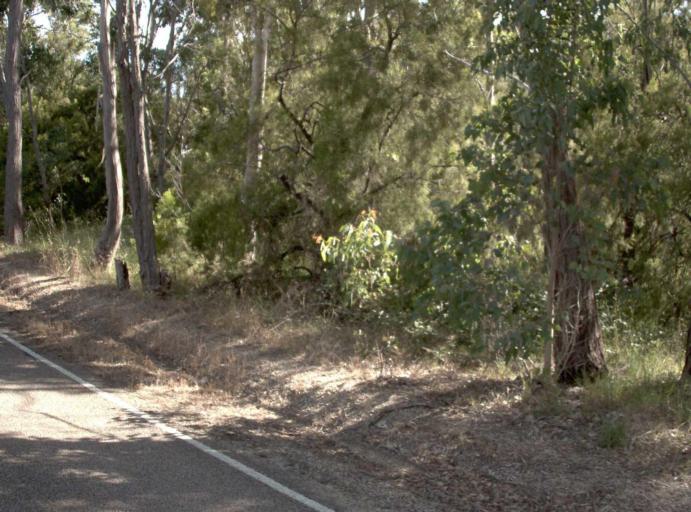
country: AU
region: Victoria
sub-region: East Gippsland
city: Lakes Entrance
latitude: -37.7895
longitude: 147.8299
